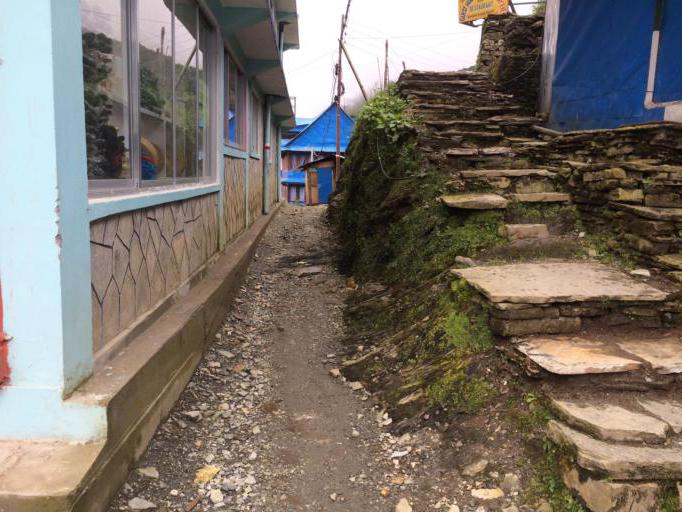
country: NP
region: Western Region
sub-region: Dhawalagiri Zone
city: Chitre
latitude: 28.4025
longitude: 83.6999
